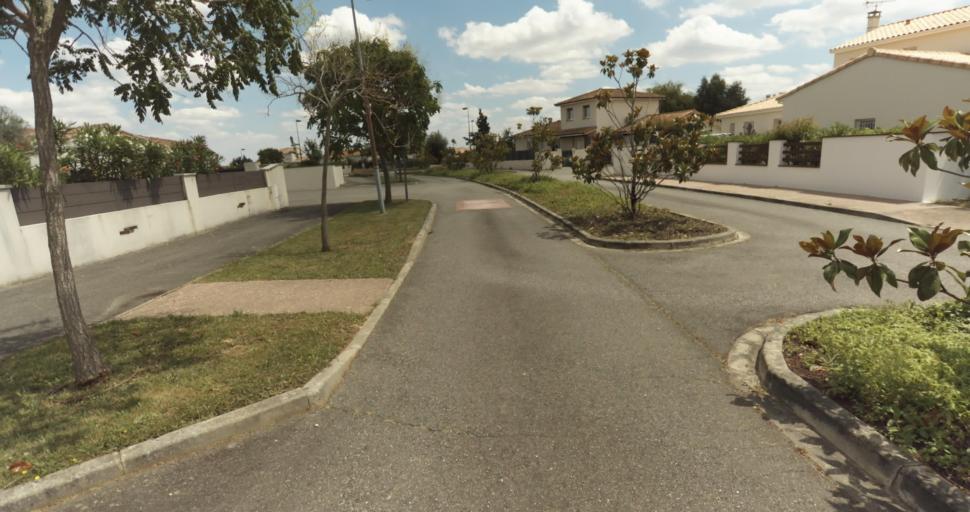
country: FR
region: Midi-Pyrenees
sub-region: Departement de la Haute-Garonne
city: Fontenilles
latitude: 43.5560
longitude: 1.1671
